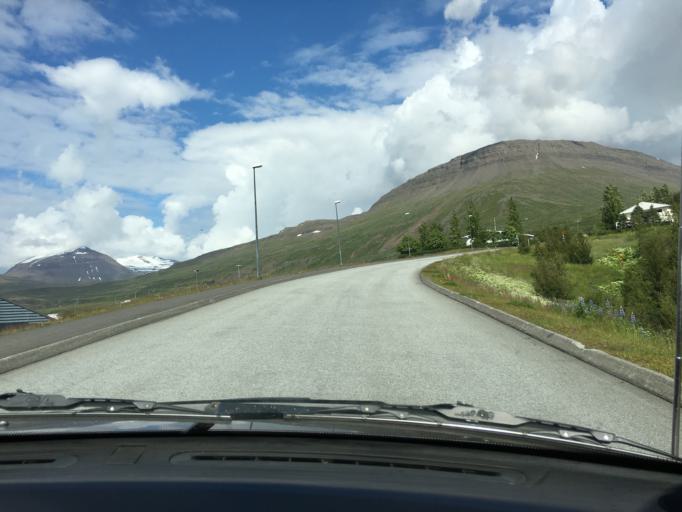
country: IS
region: East
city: Reydarfjoerdur
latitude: 65.0343
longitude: -14.2080
